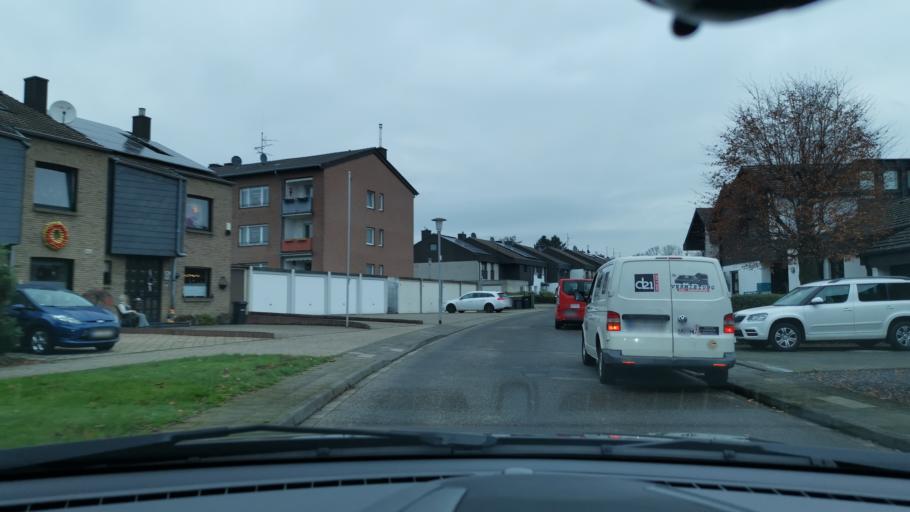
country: DE
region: North Rhine-Westphalia
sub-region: Regierungsbezirk Dusseldorf
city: Neubrueck
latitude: 51.1326
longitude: 6.6278
